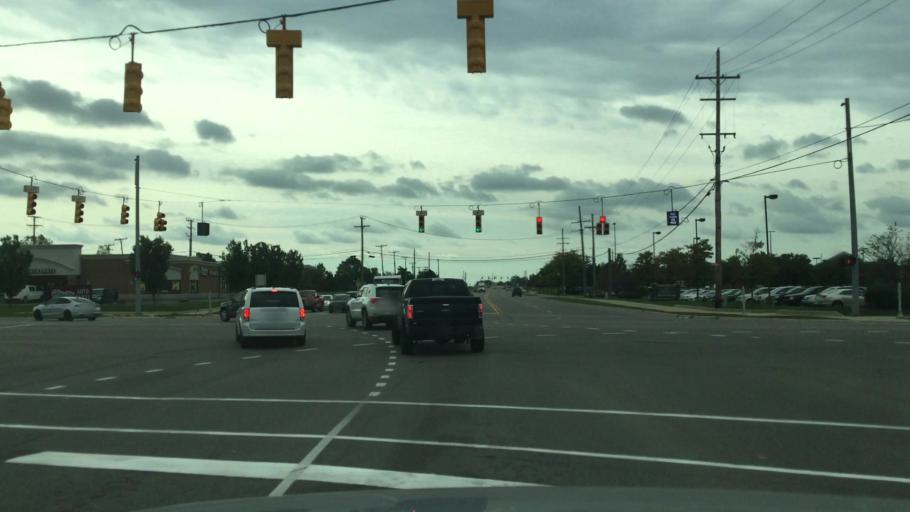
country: US
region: Michigan
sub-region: Livingston County
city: Howell
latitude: 42.5871
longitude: -83.8742
